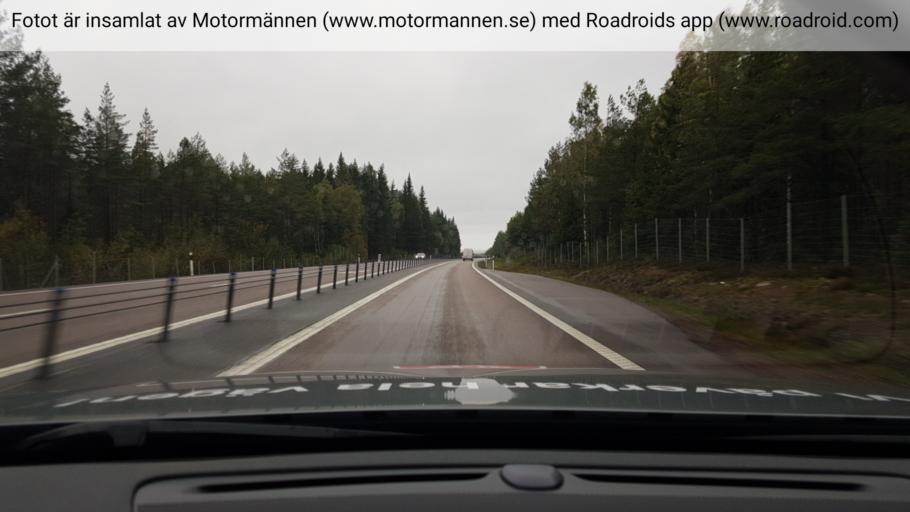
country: SE
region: Vaermland
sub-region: Kristinehamns Kommun
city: Bjorneborg
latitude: 59.3117
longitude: 14.2336
